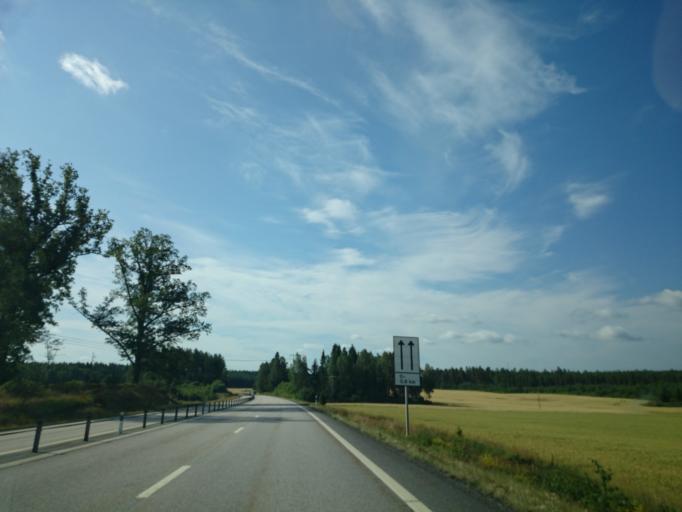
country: SE
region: Kalmar
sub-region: Vasterviks Kommun
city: Forserum
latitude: 58.0737
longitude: 16.5183
